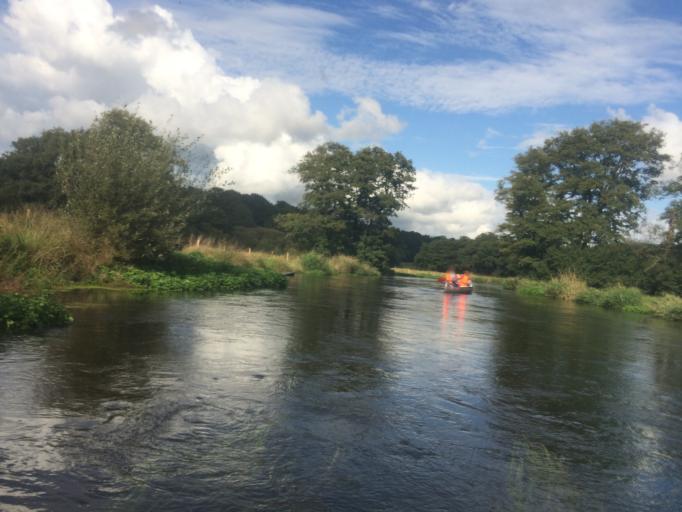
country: DK
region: South Denmark
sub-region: Vejle Kommune
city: Egtved
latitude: 55.6616
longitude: 9.3173
